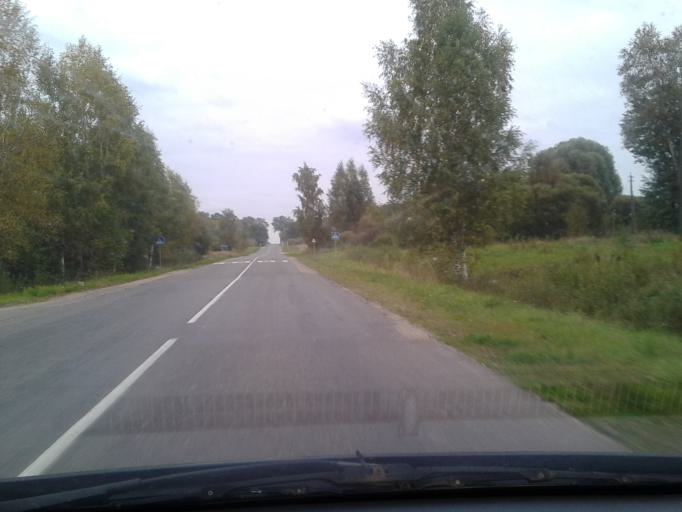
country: BY
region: Vitebsk
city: Pastavy
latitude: 55.1261
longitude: 26.9328
